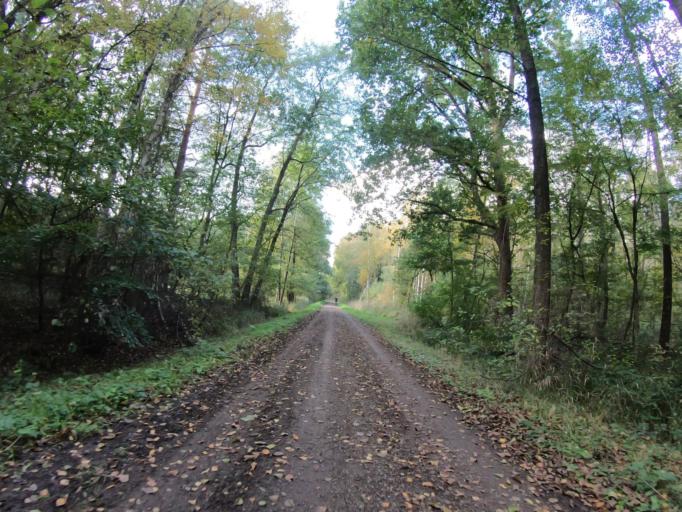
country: DE
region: Lower Saxony
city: Gifhorn
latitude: 52.5073
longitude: 10.5702
